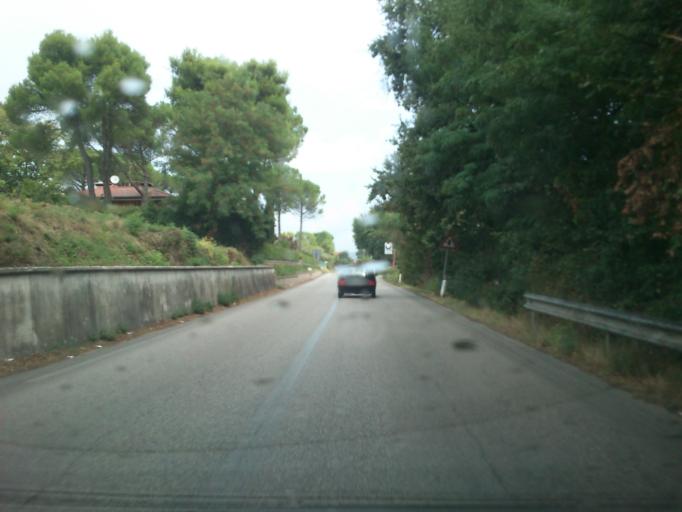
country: IT
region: The Marches
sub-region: Provincia di Pesaro e Urbino
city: Lucrezia
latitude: 43.7664
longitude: 12.9303
